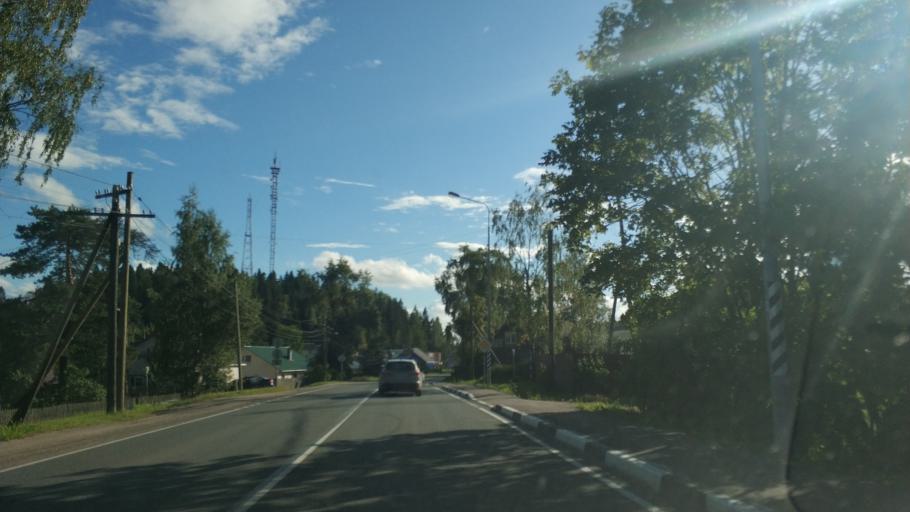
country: RU
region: Republic of Karelia
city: Lakhdenpokh'ya
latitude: 61.5283
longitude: 30.2036
